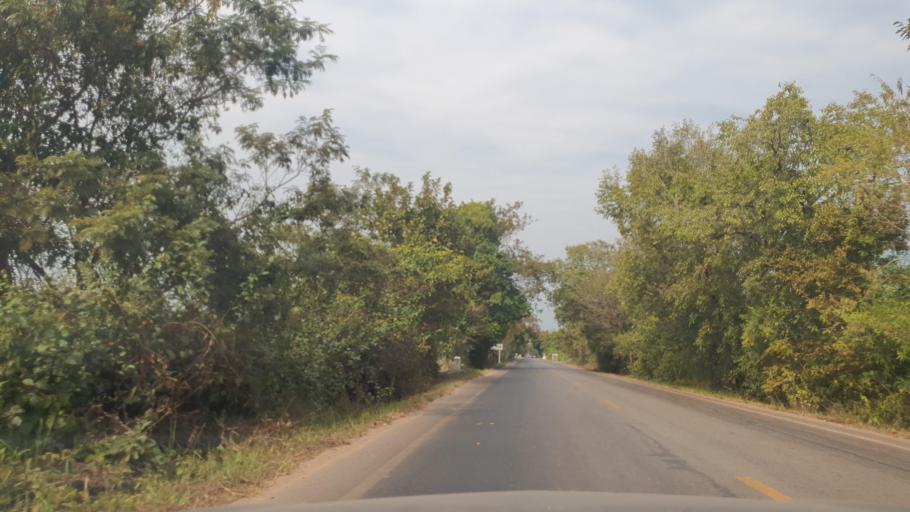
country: TH
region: Changwat Bueng Kan
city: Bung Khla
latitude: 18.2121
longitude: 104.0442
